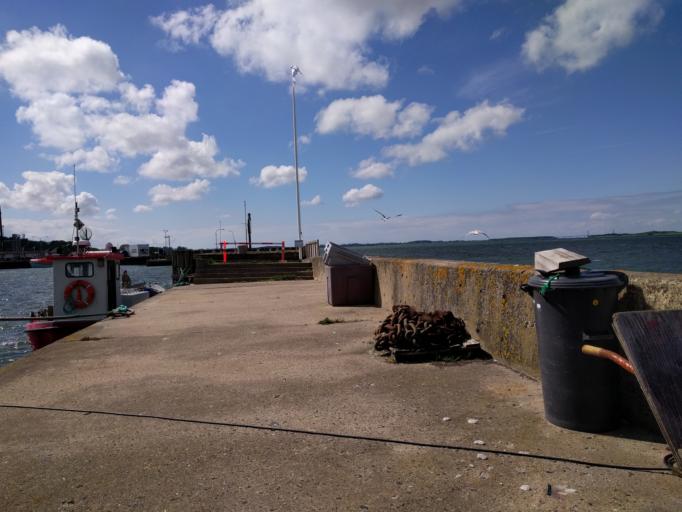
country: DK
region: Zealand
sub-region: Guldborgsund Kommune
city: Stubbekobing
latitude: 54.8924
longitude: 12.0461
